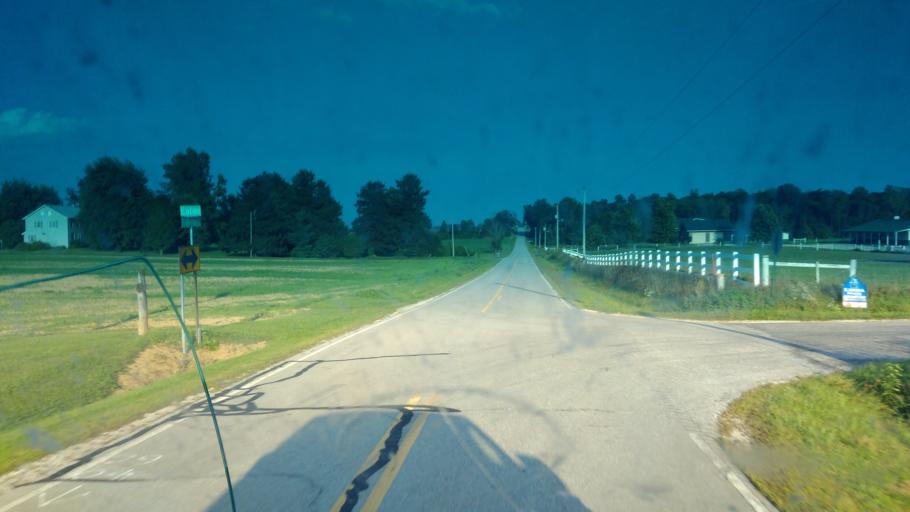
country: US
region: Ohio
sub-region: Crawford County
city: Bucyrus
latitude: 40.9067
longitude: -82.9882
